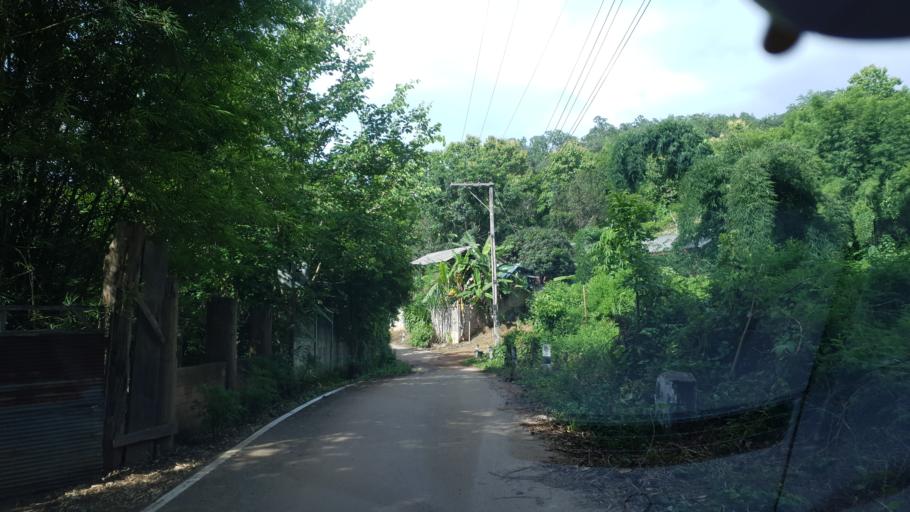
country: TH
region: Mae Hong Son
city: Khun Yuam
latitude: 18.6507
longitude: 97.9425
